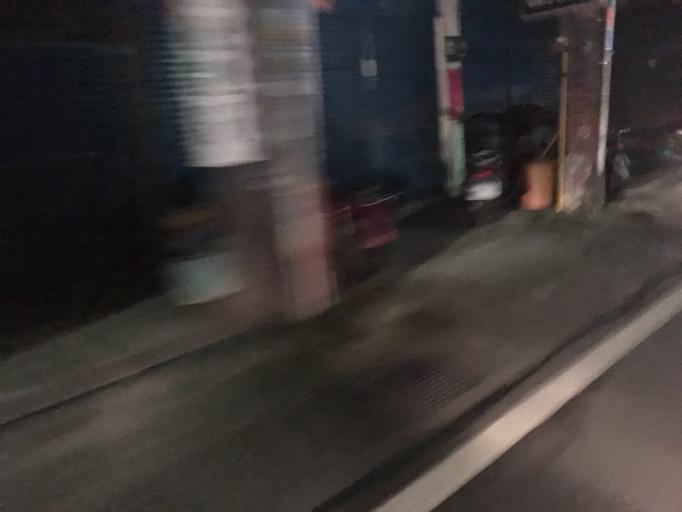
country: TW
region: Taiwan
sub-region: Hsinchu
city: Hsinchu
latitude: 24.7962
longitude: 120.9700
